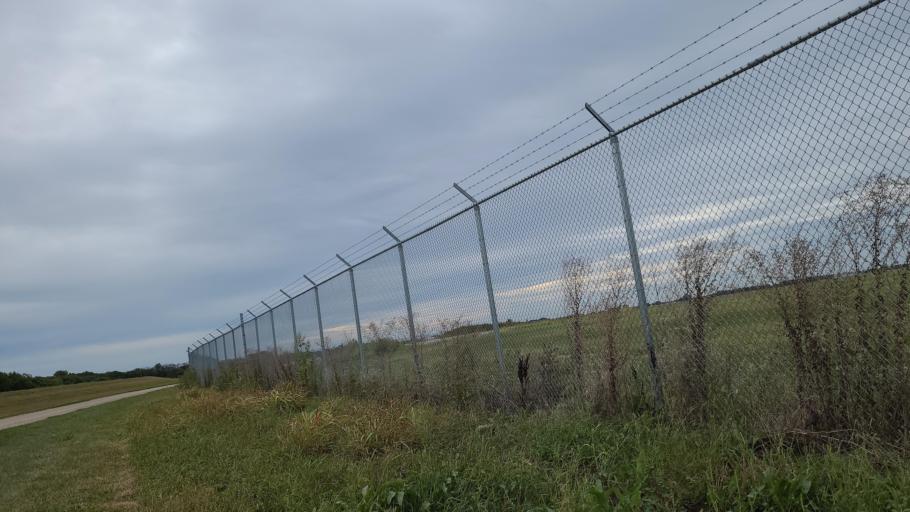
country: US
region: Kansas
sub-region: Douglas County
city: Lawrence
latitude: 39.0212
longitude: -95.2201
